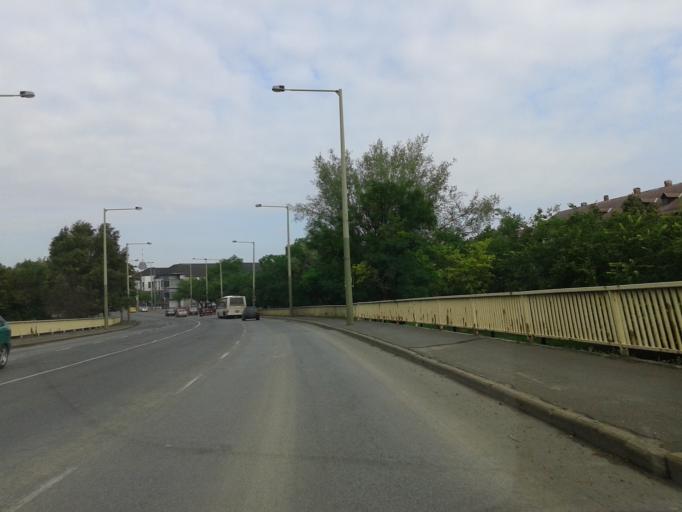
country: HU
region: Csongrad
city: Szeged
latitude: 46.2590
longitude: 20.1635
